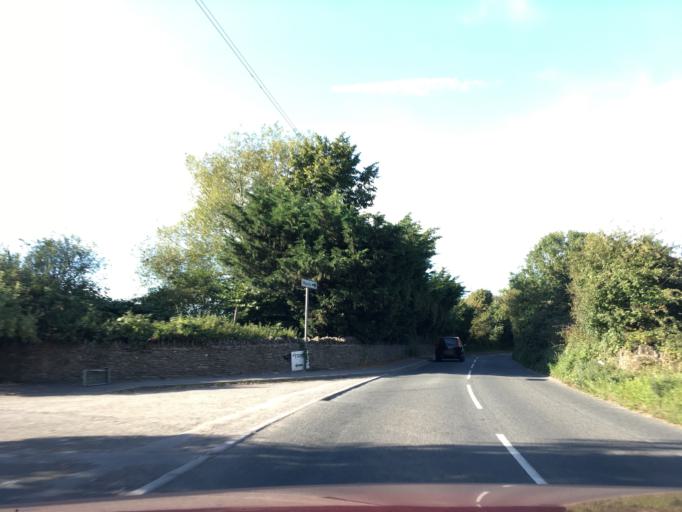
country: GB
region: England
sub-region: South Gloucestershire
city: Yate
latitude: 51.5189
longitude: -2.4346
